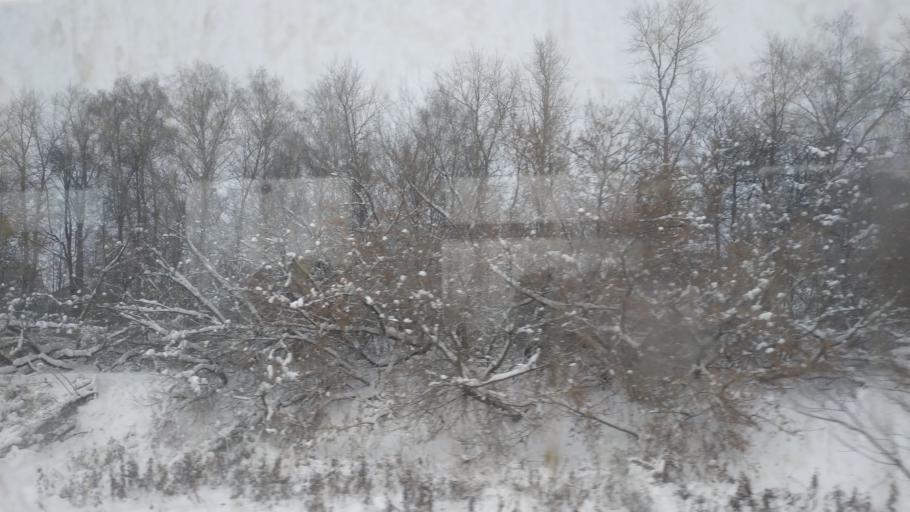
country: RU
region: Moskovskaya
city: Malyshevo
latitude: 55.5310
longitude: 38.3131
